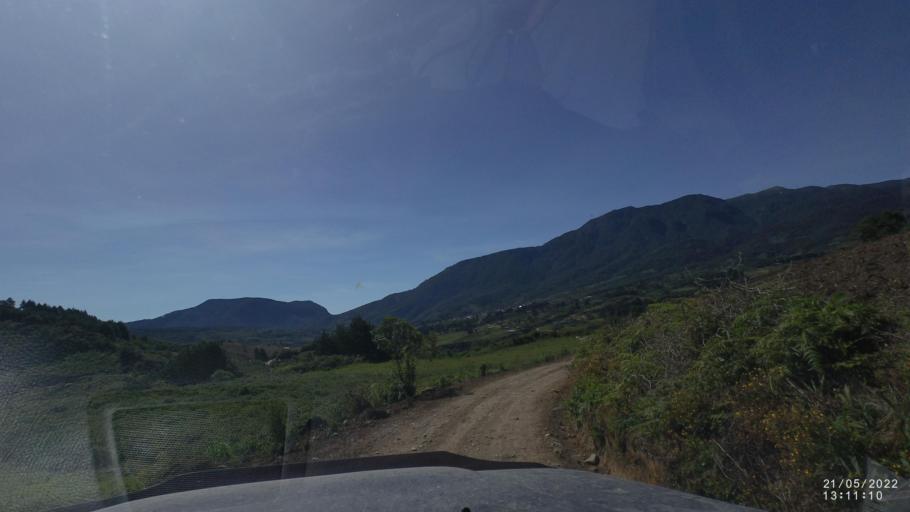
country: BO
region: Cochabamba
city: Colomi
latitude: -17.1399
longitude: -65.9433
